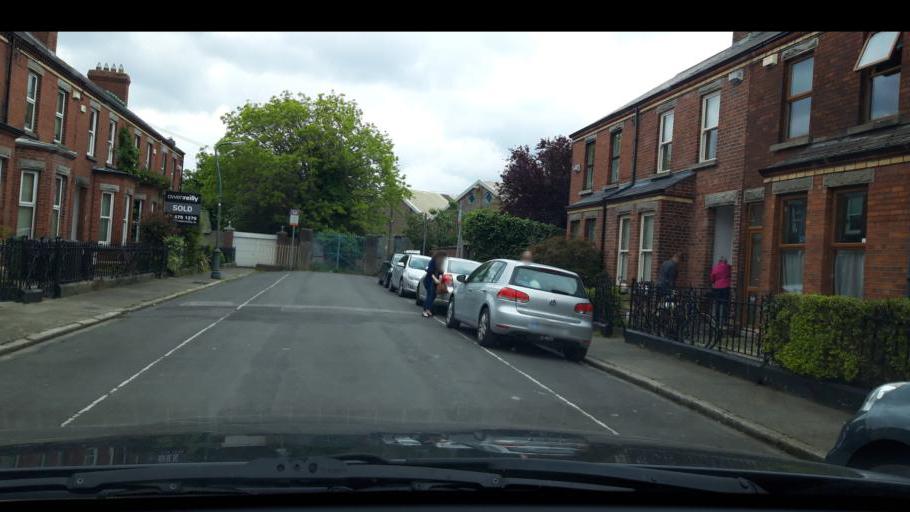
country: IE
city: Greenhills
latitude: 53.3385
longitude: -6.3028
